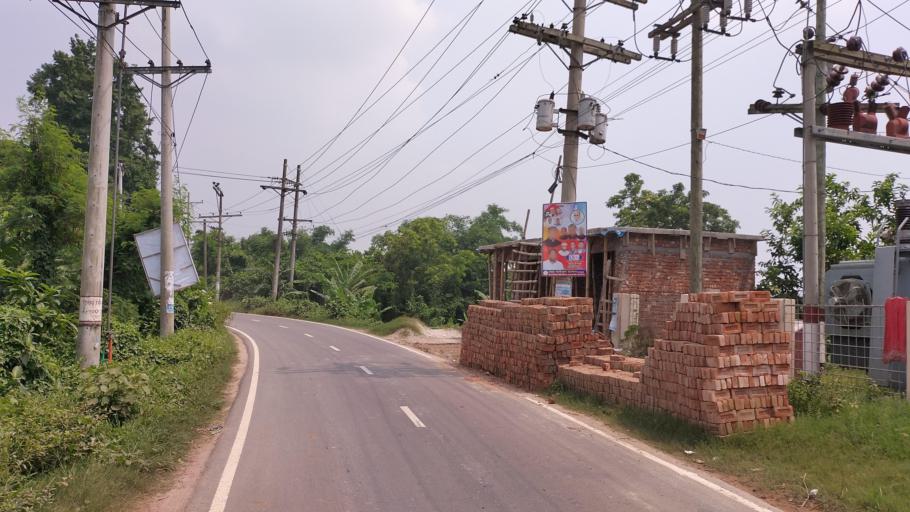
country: BD
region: Dhaka
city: Azimpur
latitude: 23.7226
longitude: 90.2741
